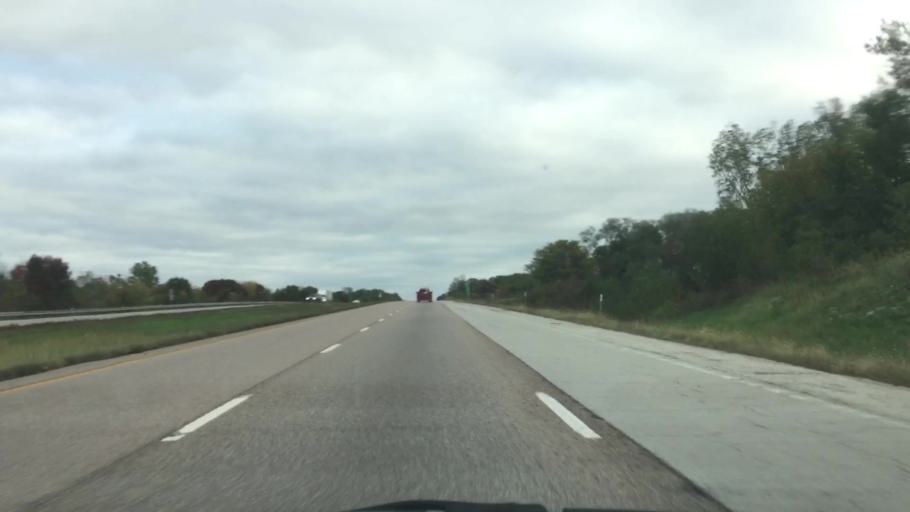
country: US
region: Missouri
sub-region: Clinton County
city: Lathrop
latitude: 39.4630
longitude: -94.3187
